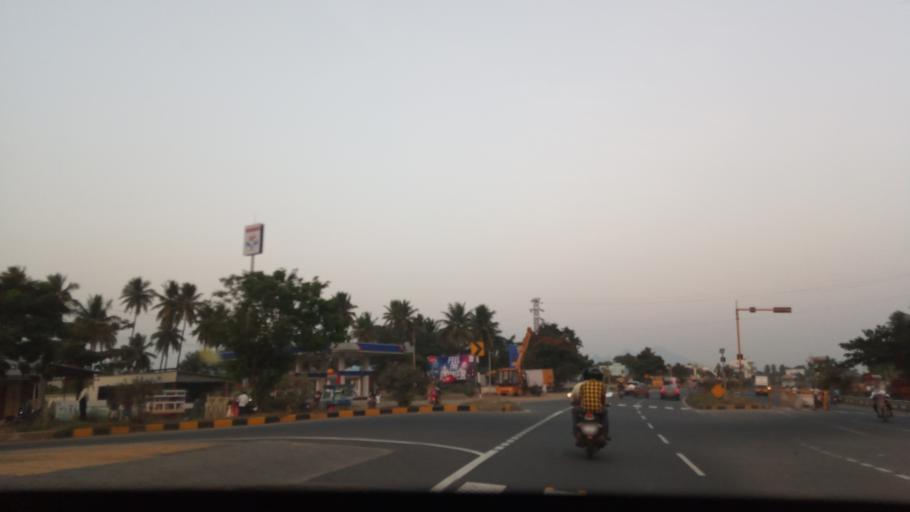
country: IN
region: Tamil Nadu
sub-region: Salem
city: Salem
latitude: 11.6671
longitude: 78.2546
